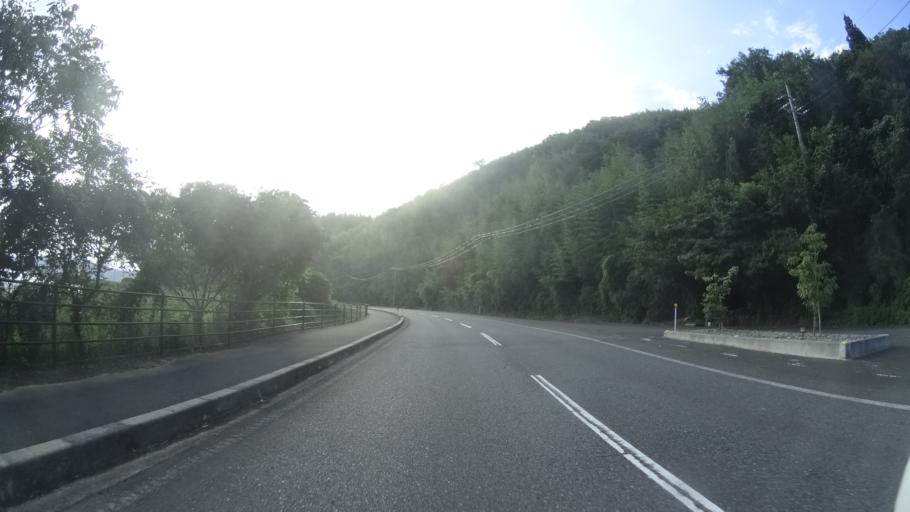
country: JP
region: Tottori
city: Kurayoshi
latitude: 35.4939
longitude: 133.8978
